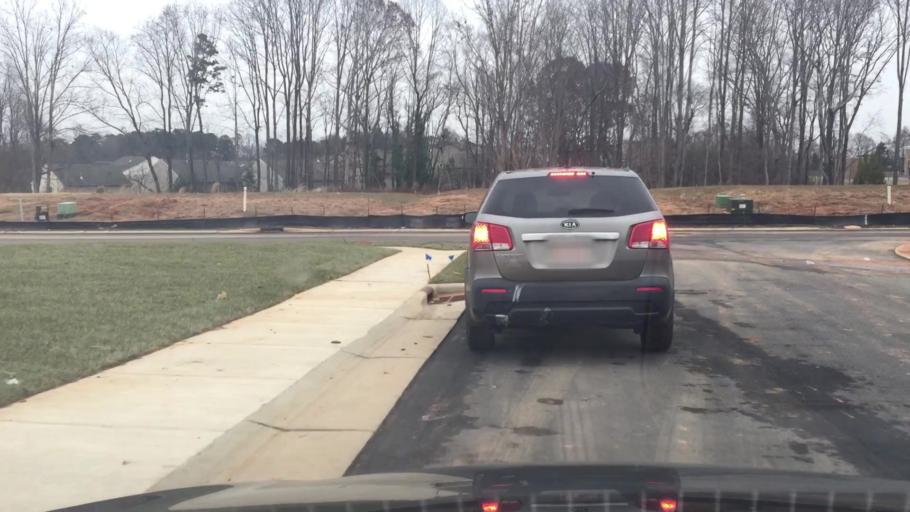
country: US
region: North Carolina
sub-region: Iredell County
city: Mooresville
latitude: 35.5795
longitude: -80.7917
